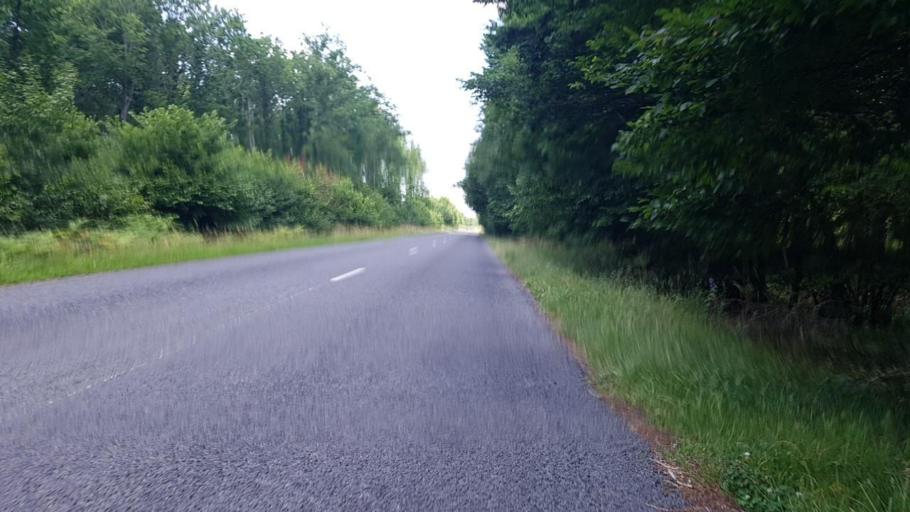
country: FR
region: Picardie
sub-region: Departement de l'Oise
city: Carlepont
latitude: 49.5179
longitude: 2.9833
